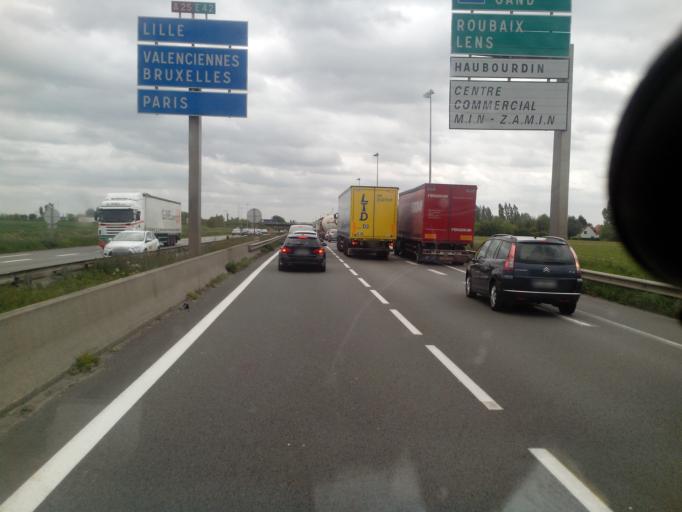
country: FR
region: Nord-Pas-de-Calais
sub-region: Departement du Nord
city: Ennetieres-en-Weppes
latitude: 50.6314
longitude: 2.9544
